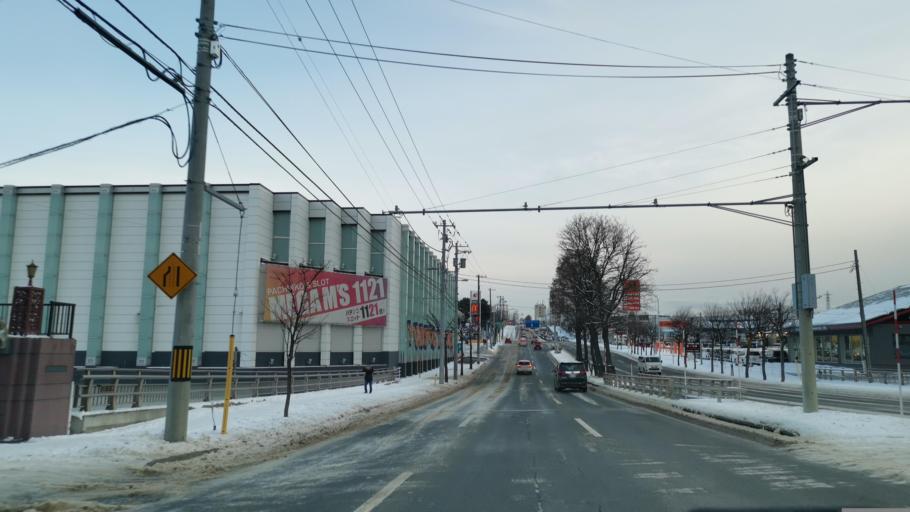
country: JP
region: Hokkaido
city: Sapporo
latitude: 43.0225
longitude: 141.3822
